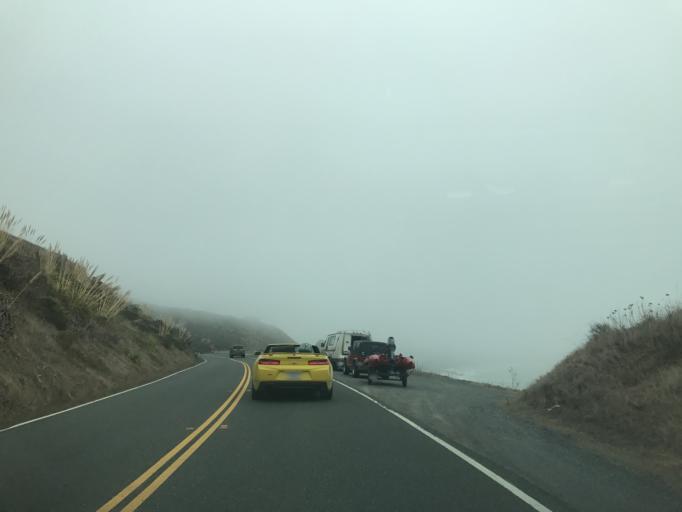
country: US
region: California
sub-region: Sonoma County
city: Monte Rio
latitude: 38.4558
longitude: -123.1361
